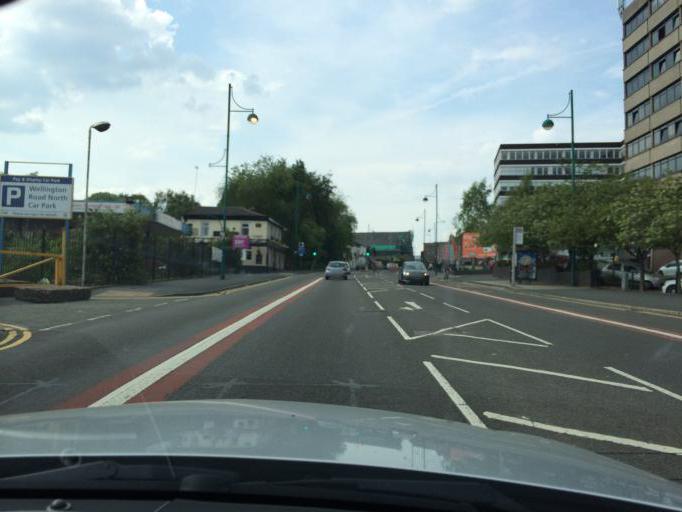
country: GB
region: England
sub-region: Borough of Stockport
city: Stockport
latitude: 53.4113
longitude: -2.1655
